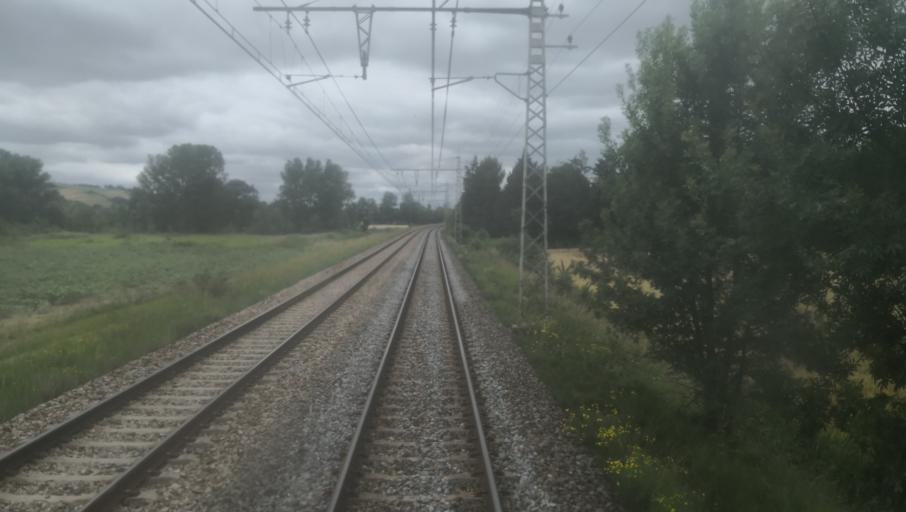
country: FR
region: Midi-Pyrenees
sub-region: Departement de la Haute-Garonne
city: Avignonet-Lauragais
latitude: 43.3690
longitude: 1.7703
